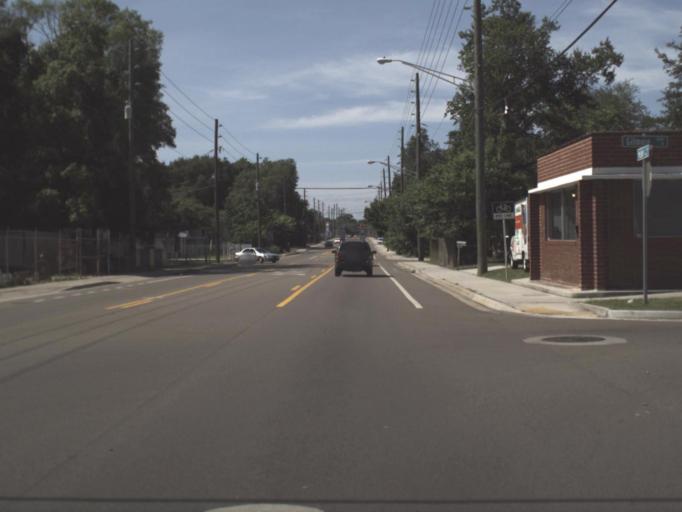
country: US
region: Florida
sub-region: Duval County
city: Jacksonville
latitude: 30.3185
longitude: -81.7055
